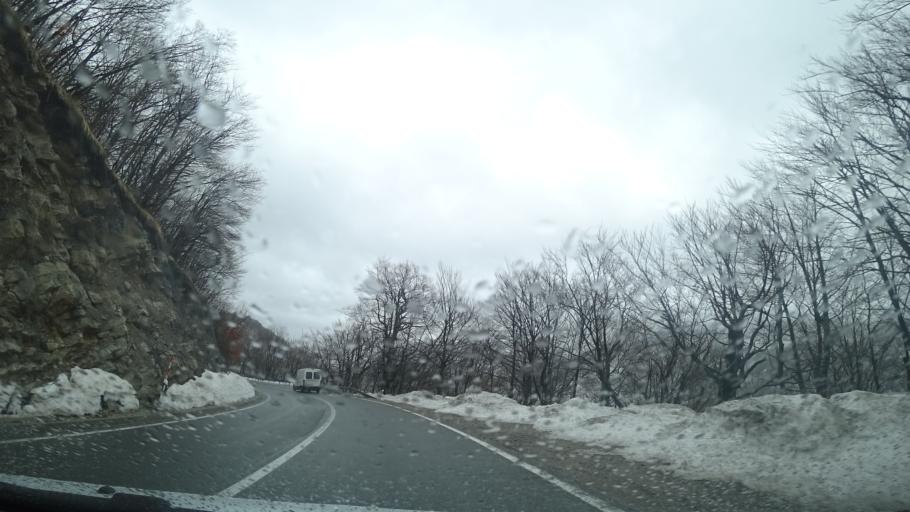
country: HR
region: Licko-Senjska
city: Popovaca
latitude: 44.5157
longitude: 15.2040
